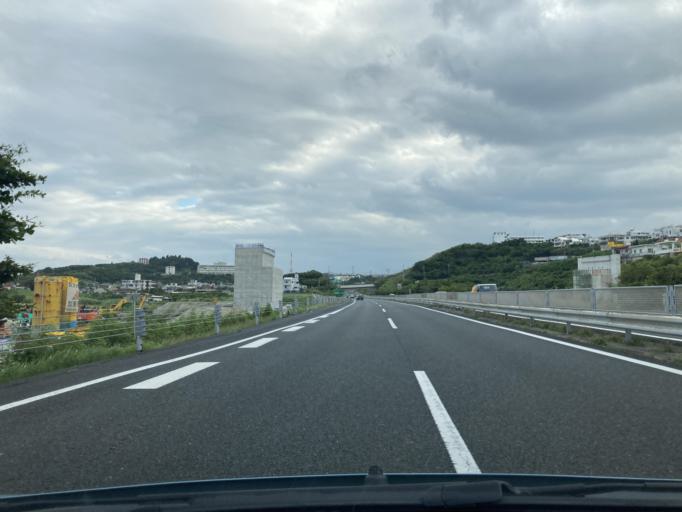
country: JP
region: Okinawa
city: Ginowan
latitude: 26.2379
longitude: 127.7413
